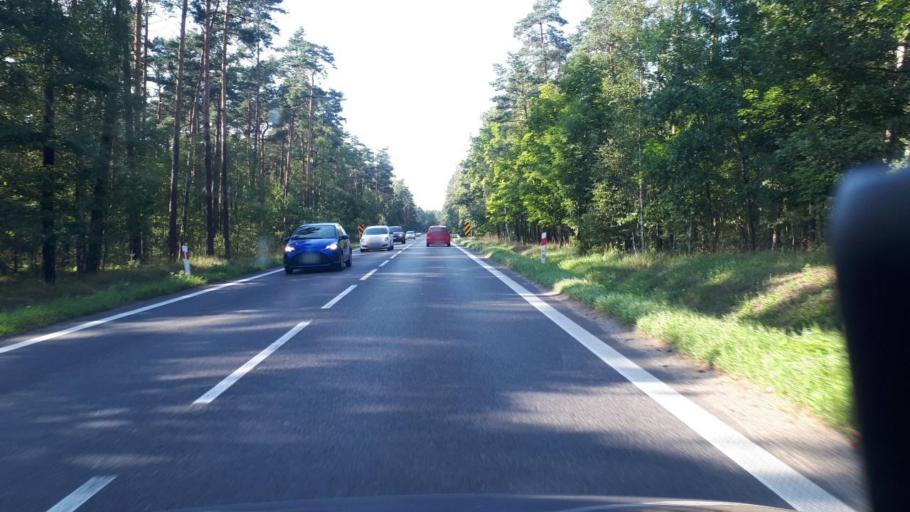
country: PL
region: Silesian Voivodeship
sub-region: Powiat lubliniecki
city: Lubliniec
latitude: 50.6193
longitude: 18.6872
